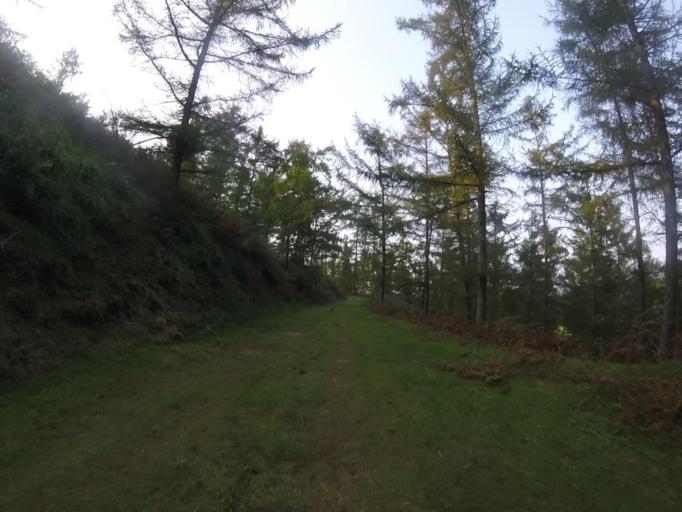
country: ES
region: Navarre
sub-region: Provincia de Navarra
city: Arano
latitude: 43.2575
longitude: -1.8381
